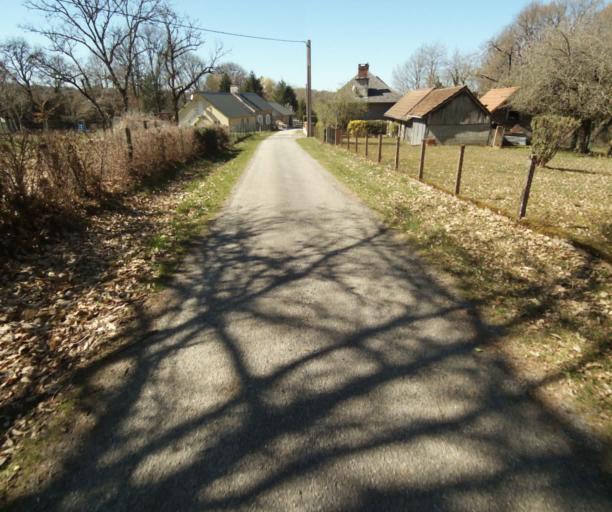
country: FR
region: Limousin
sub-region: Departement de la Correze
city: Chamboulive
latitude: 45.4021
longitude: 1.6786
